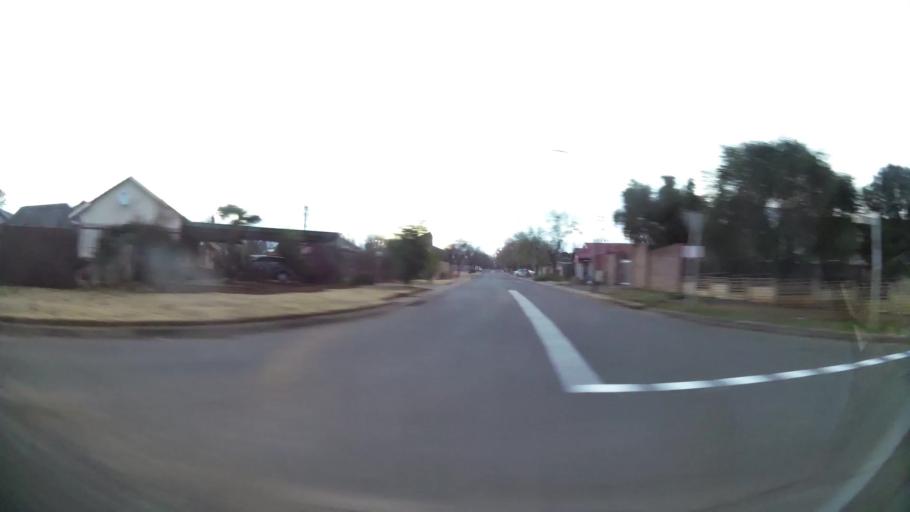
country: ZA
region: Orange Free State
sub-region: Mangaung Metropolitan Municipality
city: Bloemfontein
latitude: -29.1654
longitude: 26.1996
